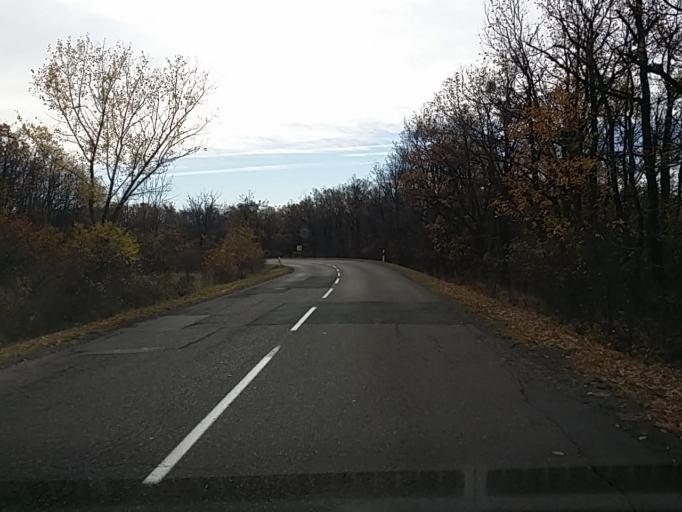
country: HU
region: Heves
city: Gyongyossolymos
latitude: 47.8502
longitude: 19.9590
